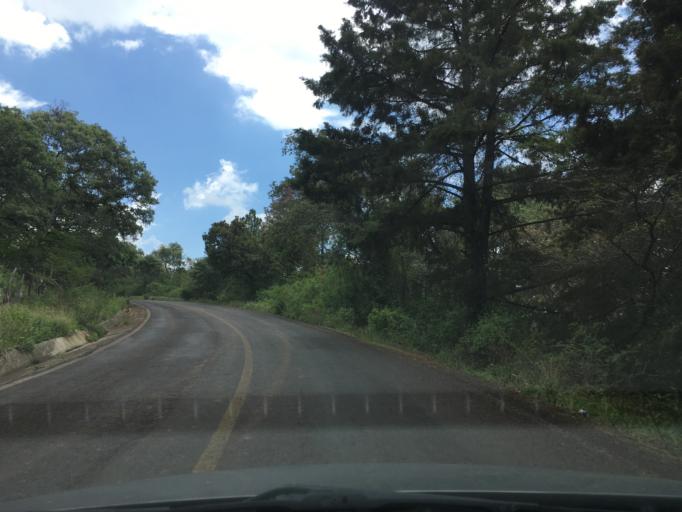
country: MX
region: Michoacan
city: Acuitzio del Canje
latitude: 19.5468
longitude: -101.2601
